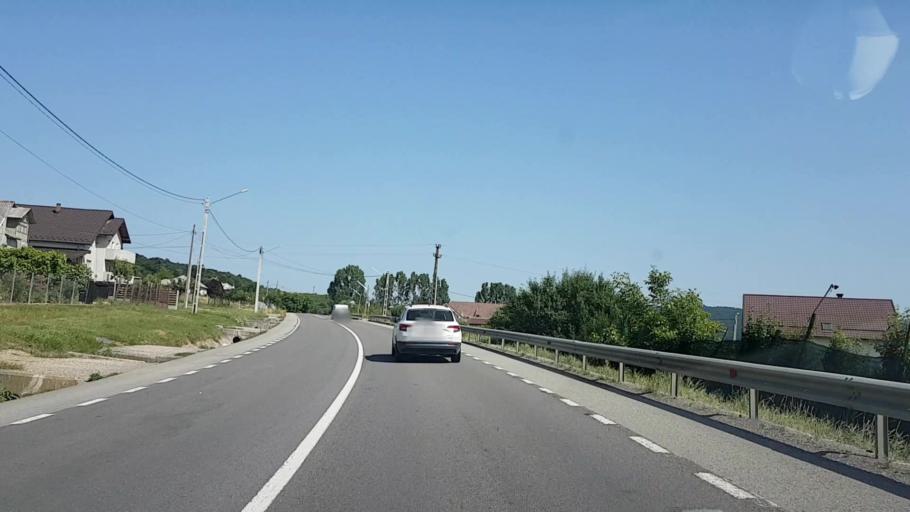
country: RO
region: Bistrita-Nasaud
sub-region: Comuna Sieu-Magherus
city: Sieu-Magherus
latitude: 47.0731
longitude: 24.4008
